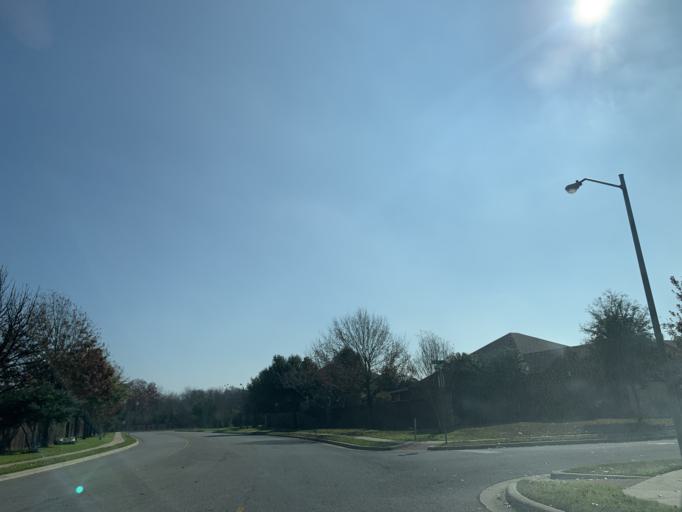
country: US
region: Texas
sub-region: Williamson County
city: Round Rock
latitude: 30.5297
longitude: -97.6416
